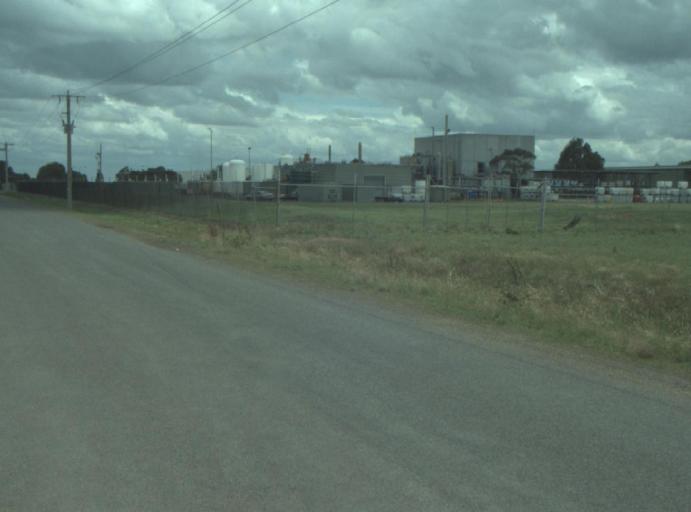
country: AU
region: Victoria
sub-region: Greater Geelong
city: Lara
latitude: -38.0484
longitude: 144.3804
